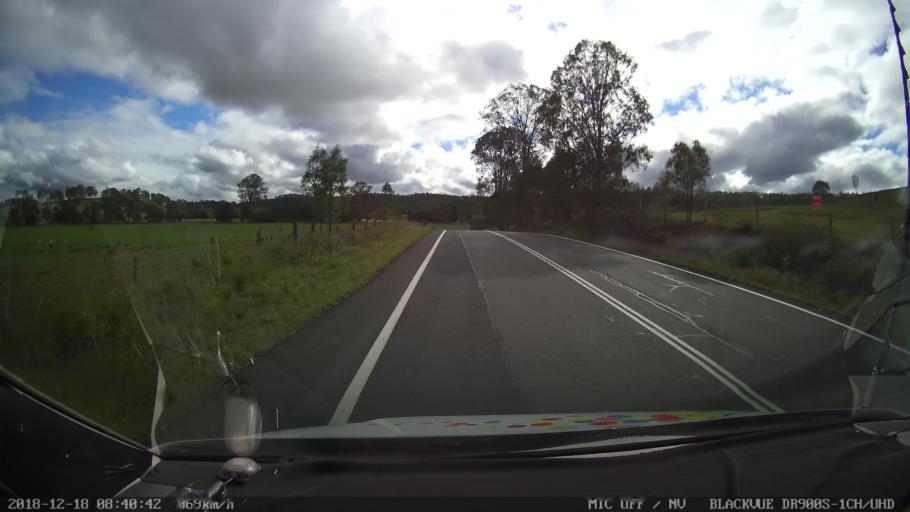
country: AU
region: Queensland
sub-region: Logan
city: Cedar Vale
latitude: -28.2410
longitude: 152.8497
